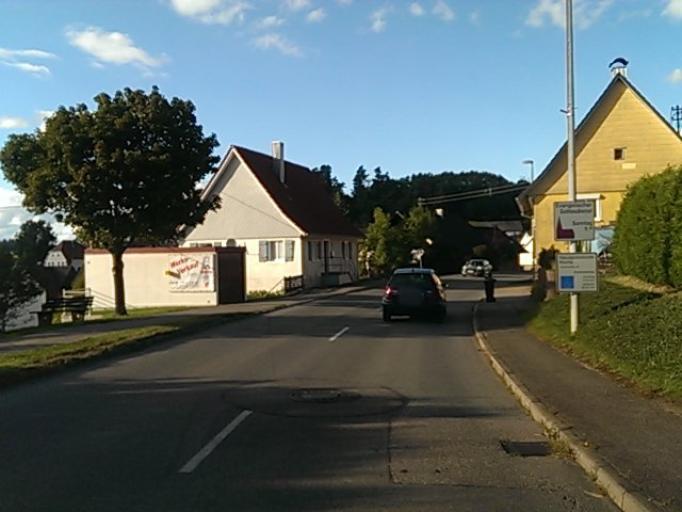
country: DE
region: Baden-Wuerttemberg
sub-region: Freiburg Region
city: Seedorf
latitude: 48.2985
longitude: 8.4886
